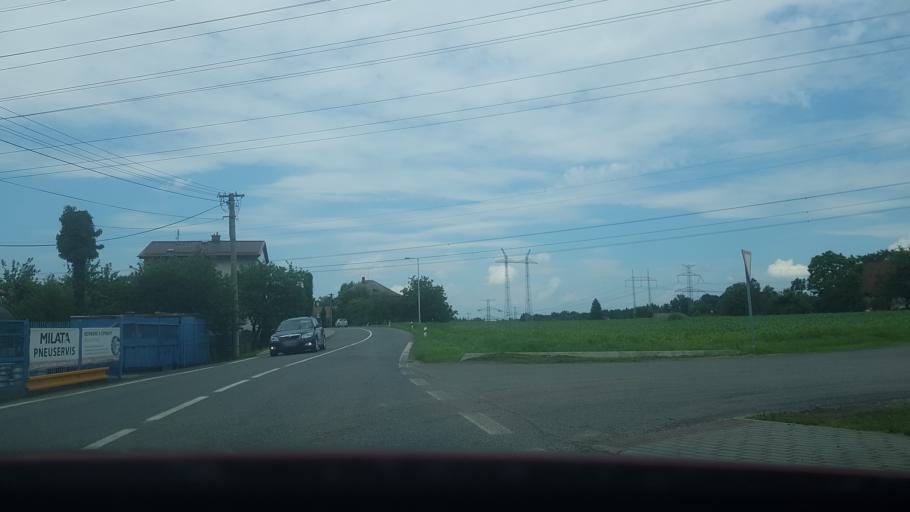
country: CZ
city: Dobra
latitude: 49.6773
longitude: 18.4251
